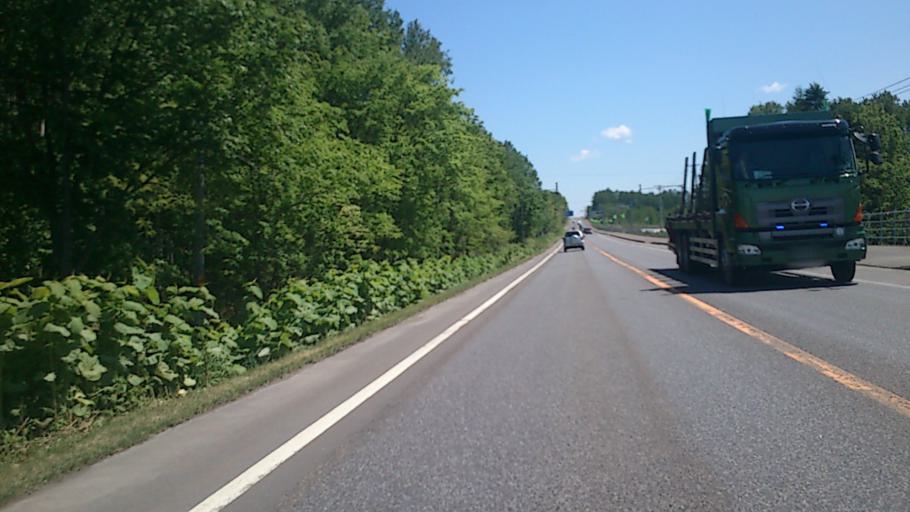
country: JP
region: Hokkaido
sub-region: Asahikawa-shi
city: Asahikawa
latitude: 44.0617
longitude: 142.4026
